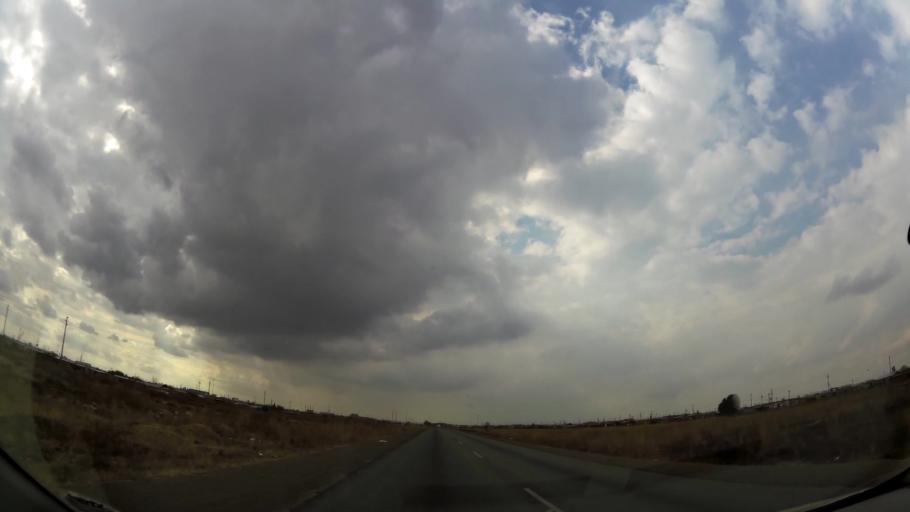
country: ZA
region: Orange Free State
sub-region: Fezile Dabi District Municipality
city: Sasolburg
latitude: -26.8621
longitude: 27.8880
